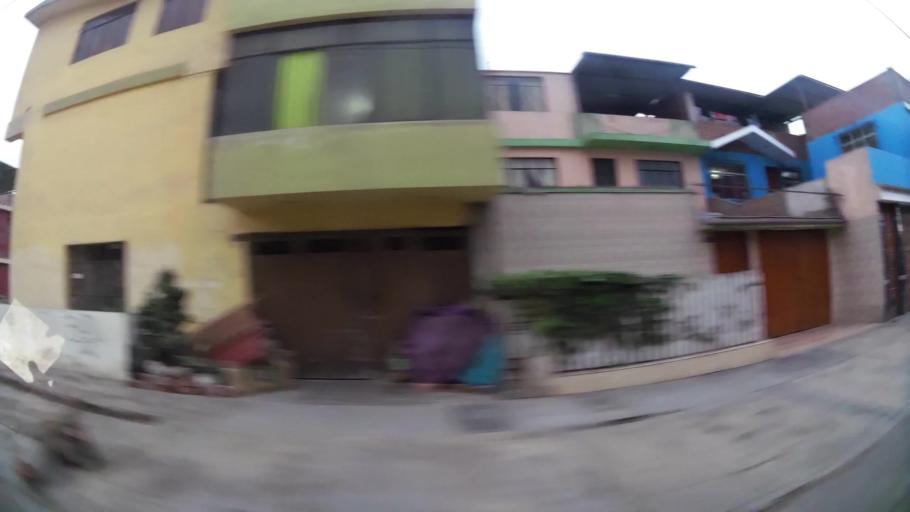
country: PE
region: Lima
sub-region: Lima
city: Surco
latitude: -12.1663
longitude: -76.9700
